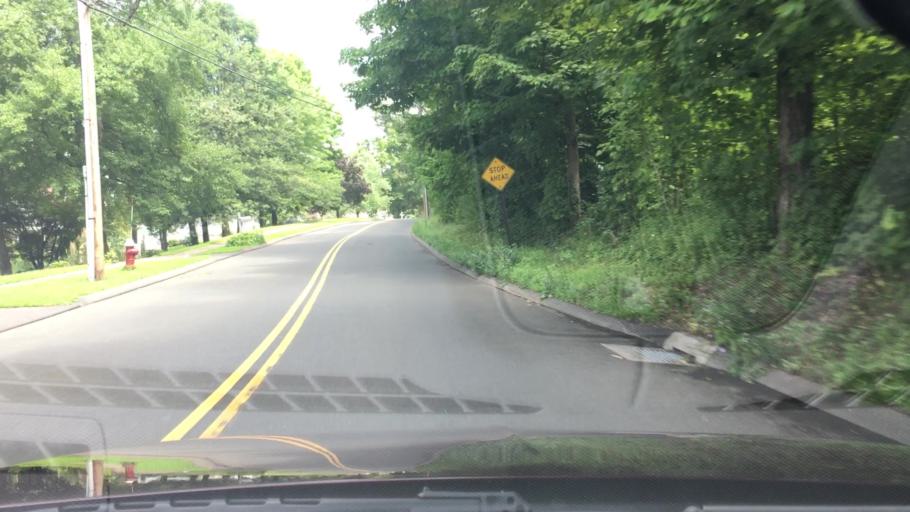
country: US
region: Connecticut
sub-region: Hartford County
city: Kensington
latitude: 41.6376
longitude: -72.7242
